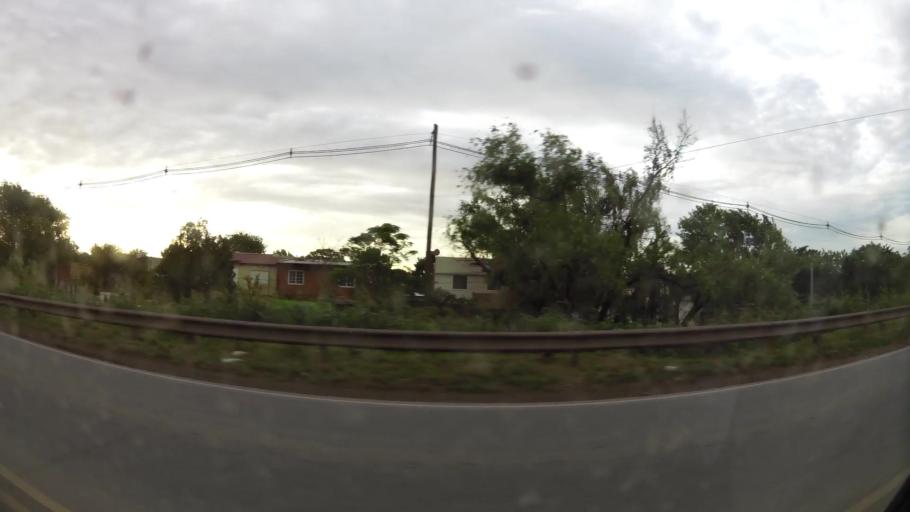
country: AR
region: Buenos Aires
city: San Nicolas de los Arroyos
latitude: -33.3670
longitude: -60.1968
